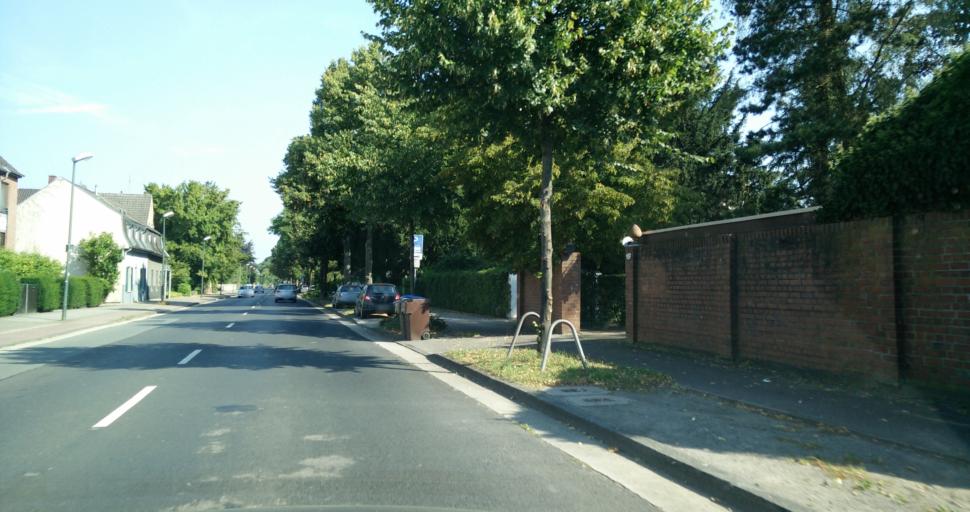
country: DE
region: North Rhine-Westphalia
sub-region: Regierungsbezirk Dusseldorf
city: Meerbusch
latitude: 51.3081
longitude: 6.7431
